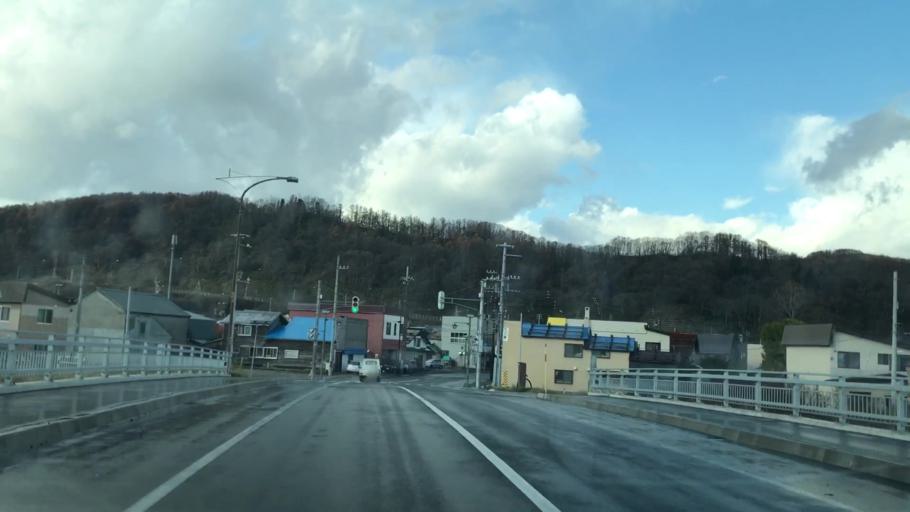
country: JP
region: Hokkaido
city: Yoichi
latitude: 43.2954
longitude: 140.6028
